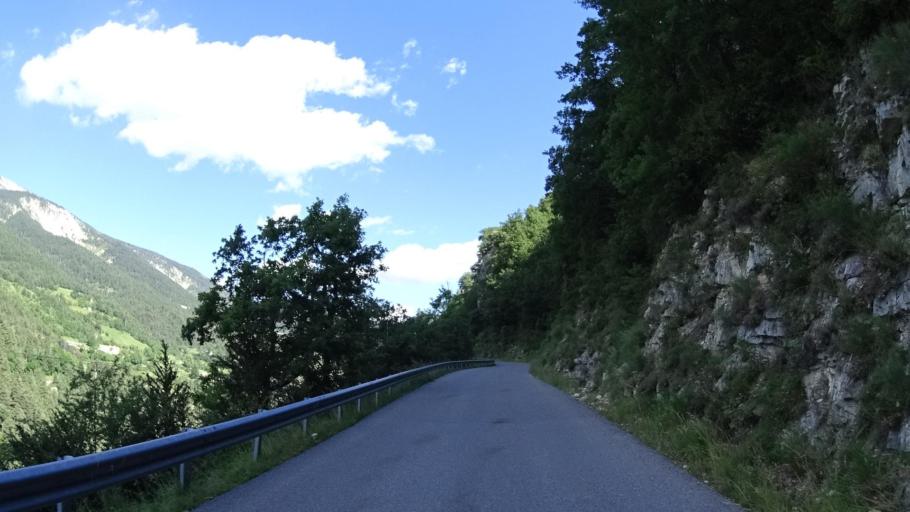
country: FR
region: Provence-Alpes-Cote d'Azur
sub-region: Departement des Alpes-de-Haute-Provence
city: Annot
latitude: 44.0158
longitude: 6.6345
